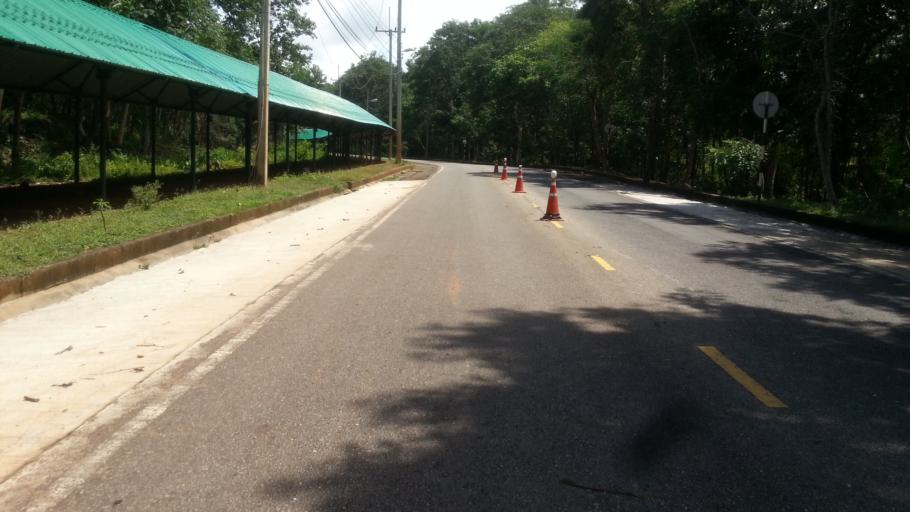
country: TH
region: Kanchanaburi
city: Sai Yok
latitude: 14.1244
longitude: 99.1549
